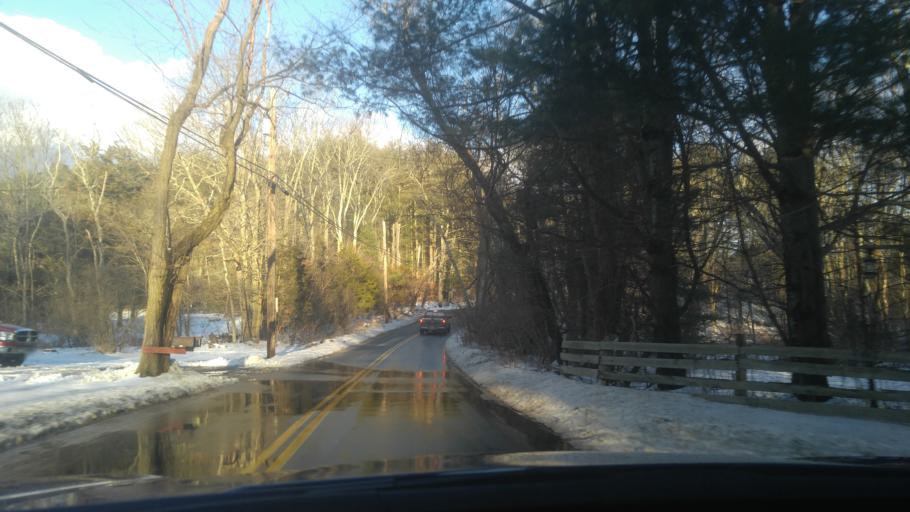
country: US
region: Rhode Island
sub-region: Kent County
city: Coventry
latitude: 41.7192
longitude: -71.6643
